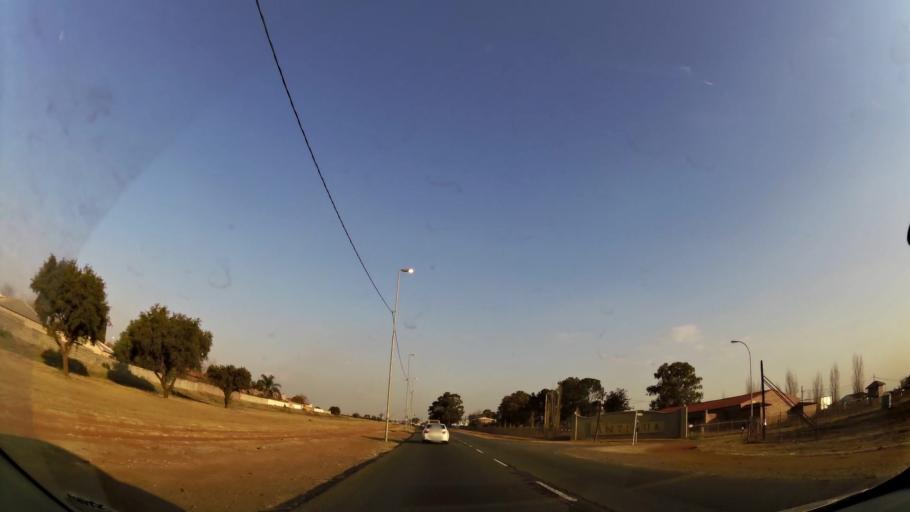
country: ZA
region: Gauteng
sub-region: Ekurhuleni Metropolitan Municipality
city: Germiston
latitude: -26.2823
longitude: 28.2270
